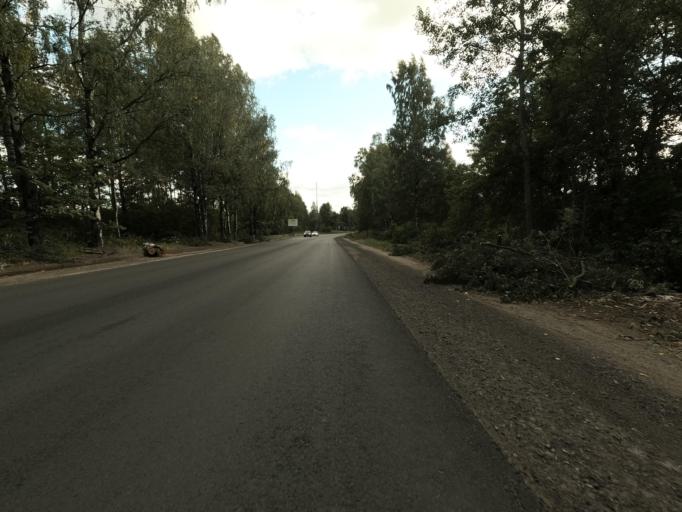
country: RU
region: Leningrad
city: Koltushi
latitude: 59.9489
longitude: 30.6573
